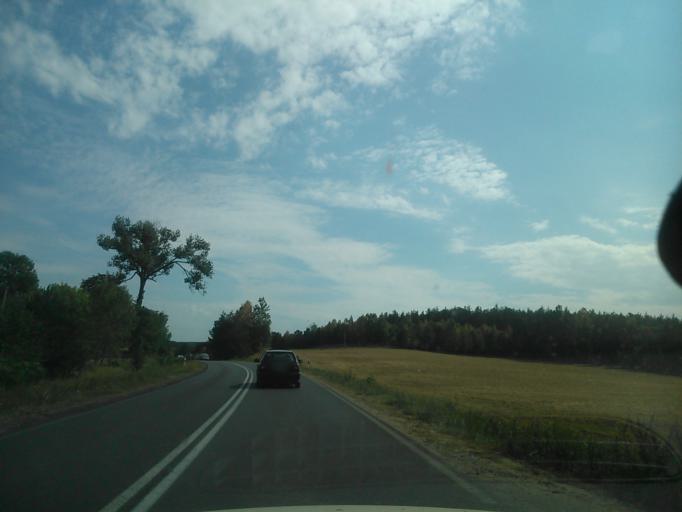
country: PL
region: Warmian-Masurian Voivodeship
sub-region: Powiat dzialdowski
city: Ilowo -Osada
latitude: 53.1511
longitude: 20.3250
